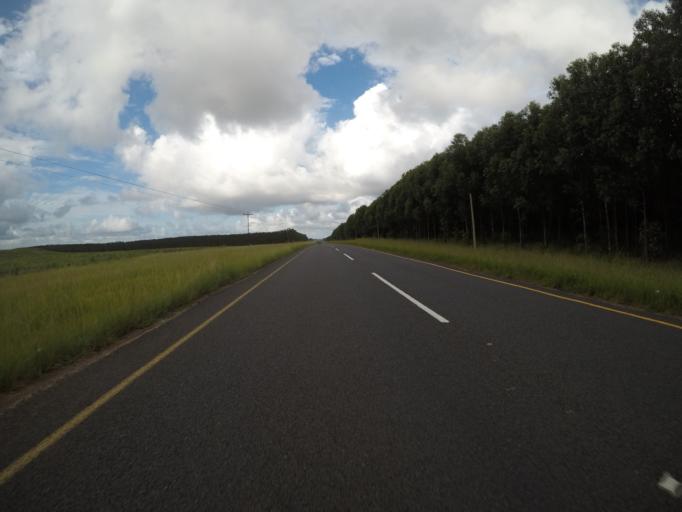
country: ZA
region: KwaZulu-Natal
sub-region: uMkhanyakude District Municipality
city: Mtubatuba
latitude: -28.3908
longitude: 32.2271
